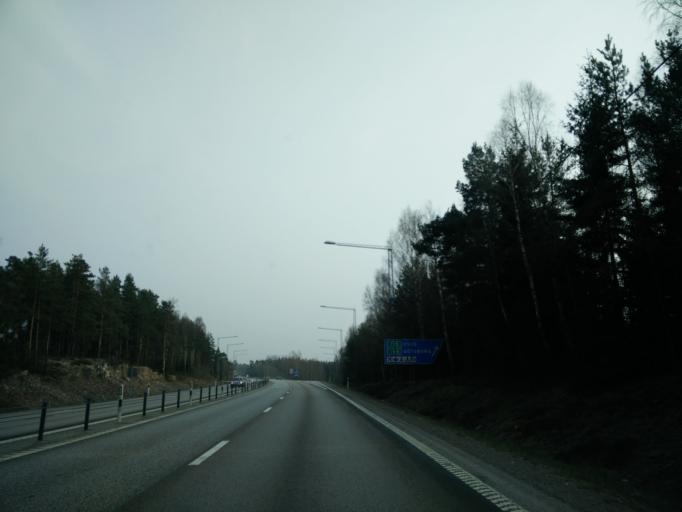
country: SE
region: Vaermland
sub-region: Hammaro Kommun
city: Skoghall
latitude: 59.3852
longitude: 13.4228
